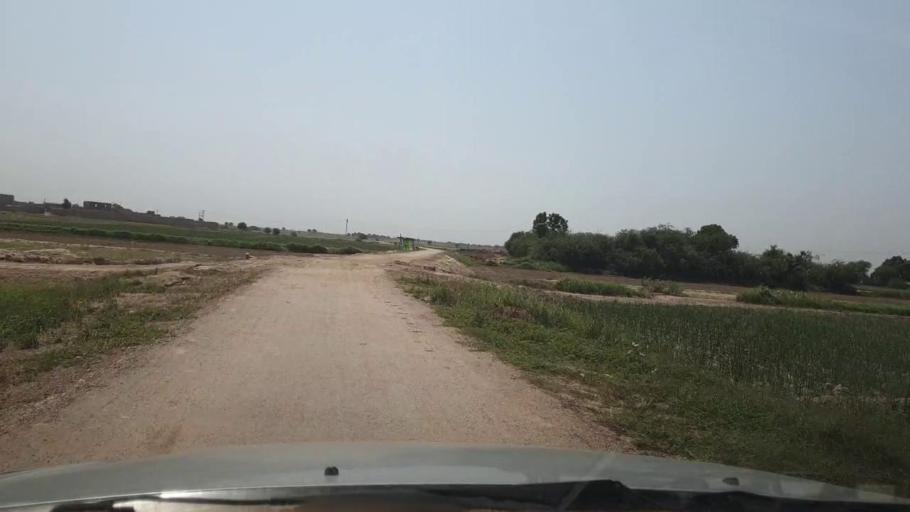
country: PK
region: Sindh
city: Chambar
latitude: 25.2620
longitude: 68.7570
